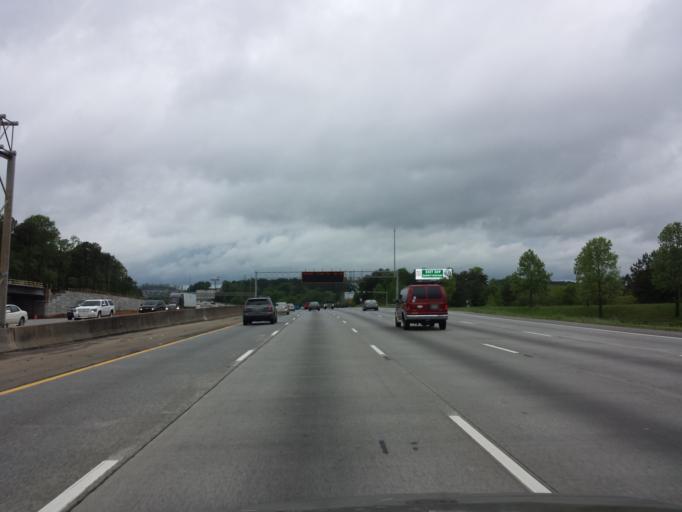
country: US
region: Georgia
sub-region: Cobb County
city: Marietta
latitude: 33.9862
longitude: -84.5436
